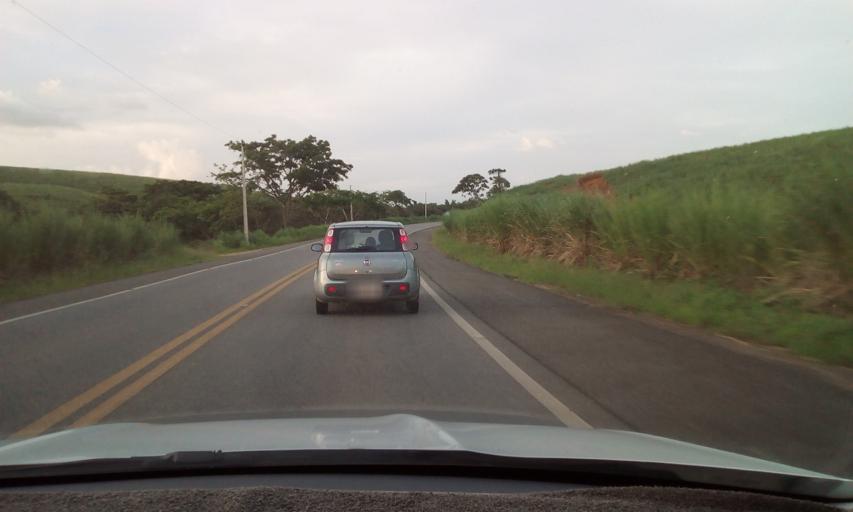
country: BR
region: Pernambuco
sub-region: Vicencia
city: Vicencia
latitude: -7.6412
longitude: -35.2546
